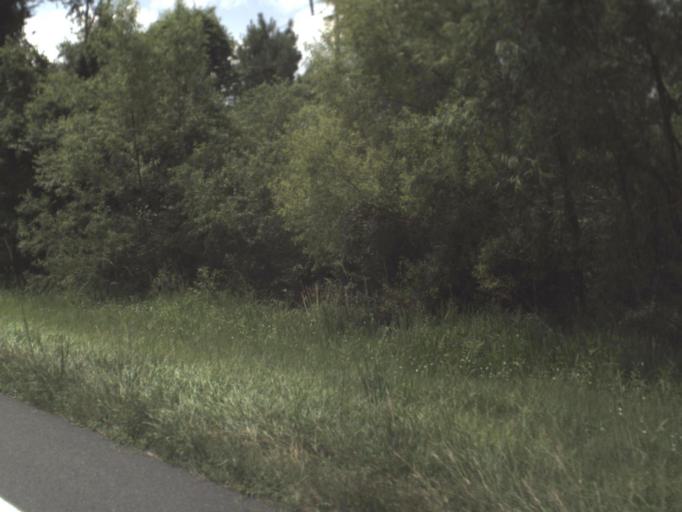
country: US
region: Florida
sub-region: Hamilton County
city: Jasper
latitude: 30.4615
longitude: -82.8977
